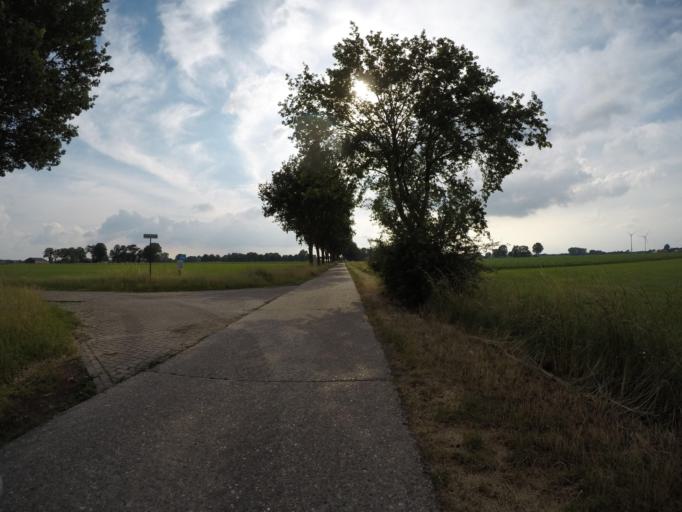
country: BE
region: Flanders
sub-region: Provincie Antwerpen
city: Brecht
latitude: 51.3588
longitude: 4.6772
